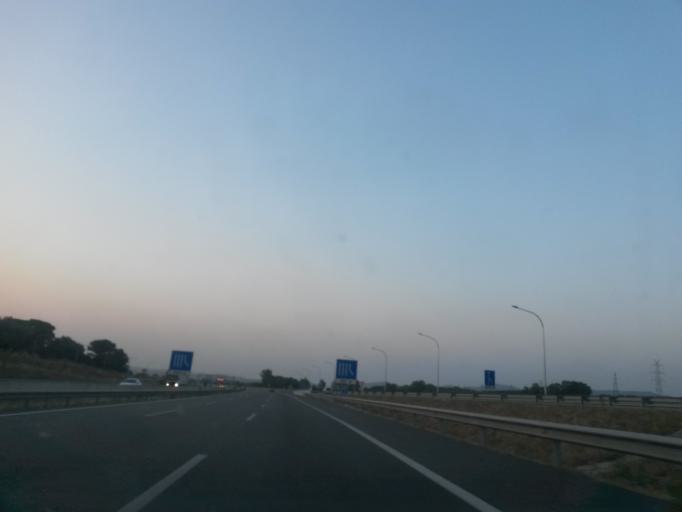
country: ES
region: Catalonia
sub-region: Provincia de Girona
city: Fornells de la Selva
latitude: 41.9345
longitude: 2.7873
